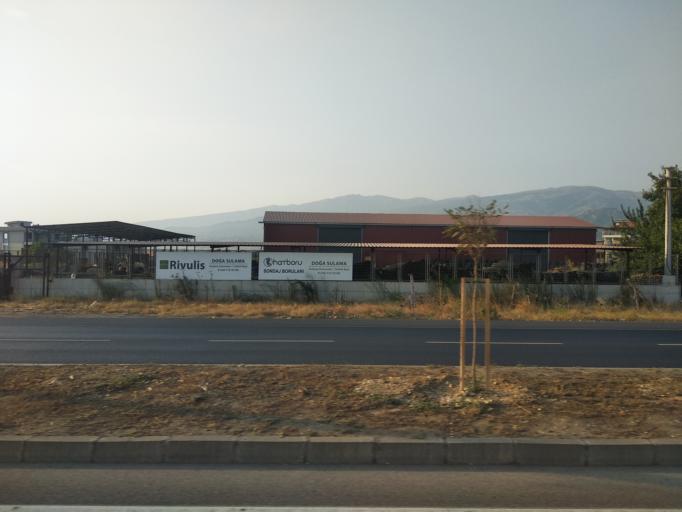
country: TR
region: Manisa
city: Salihli
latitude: 38.4956
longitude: 28.1837
